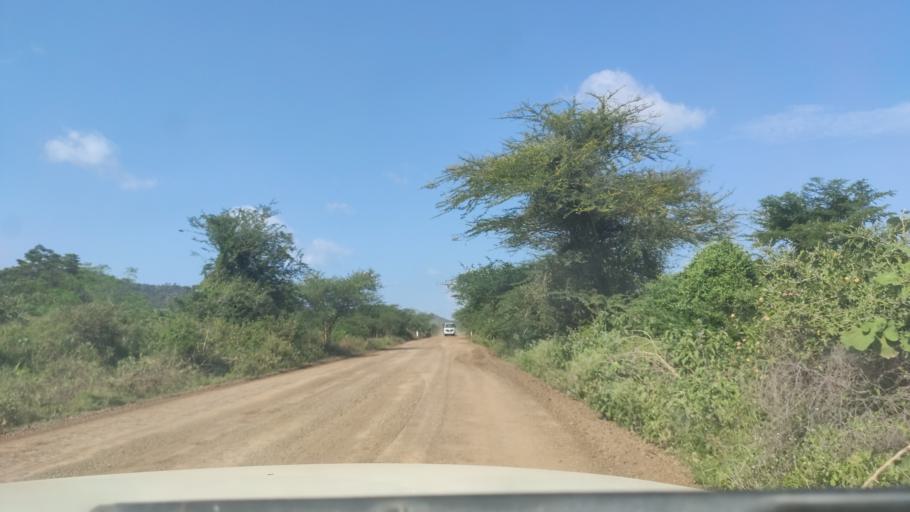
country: ET
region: Southern Nations, Nationalities, and People's Region
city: Felege Neway
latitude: 6.3903
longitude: 37.0984
